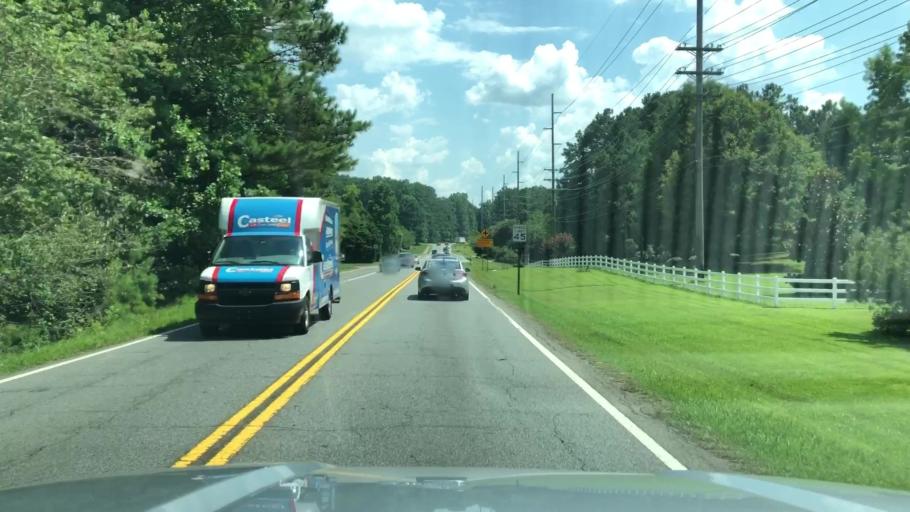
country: US
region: Georgia
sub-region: Cobb County
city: Acworth
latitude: 34.0105
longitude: -84.6990
